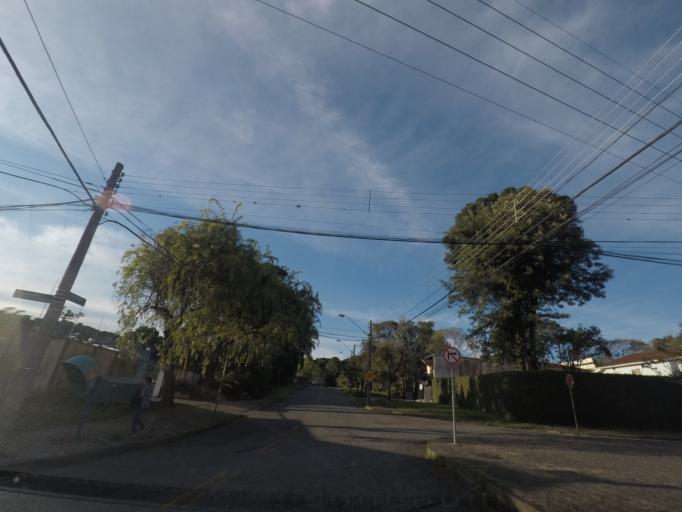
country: BR
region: Parana
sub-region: Curitiba
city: Curitiba
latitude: -25.4050
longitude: -49.2669
